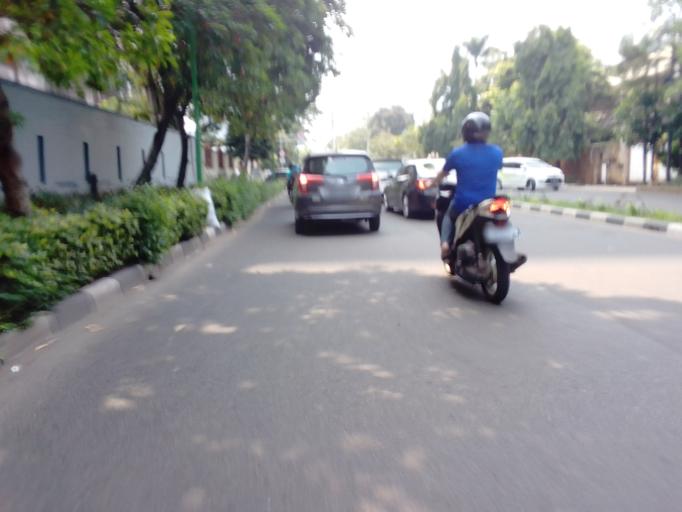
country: ID
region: Jakarta Raya
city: Jakarta
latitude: -6.2233
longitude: 106.7933
